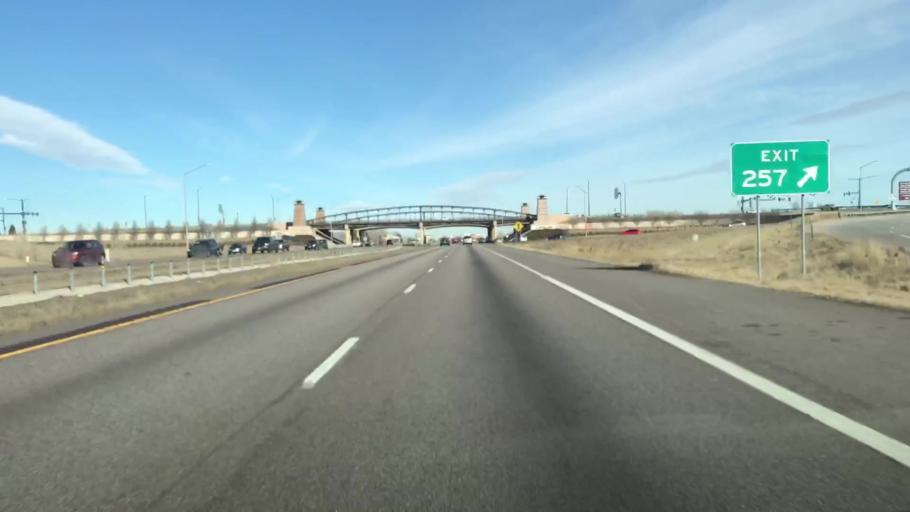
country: US
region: Colorado
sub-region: Larimer County
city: Loveland
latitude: 40.4046
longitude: -104.9931
